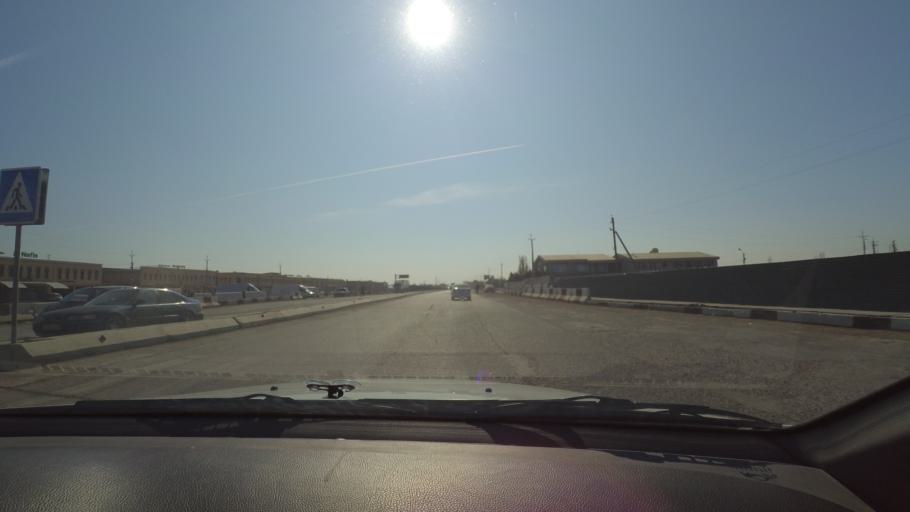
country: UZ
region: Bukhara
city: Bukhara
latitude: 39.8083
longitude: 64.4191
